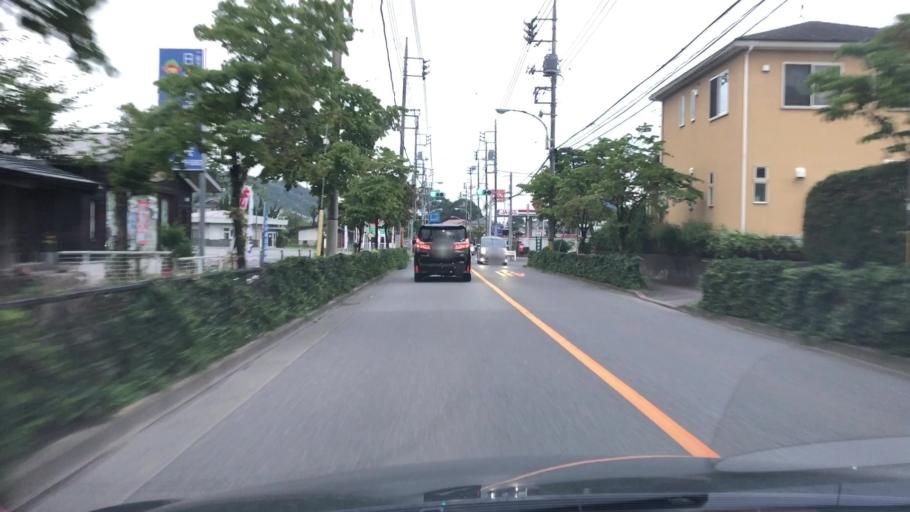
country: JP
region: Tokyo
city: Itsukaichi
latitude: 35.7428
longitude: 139.2522
